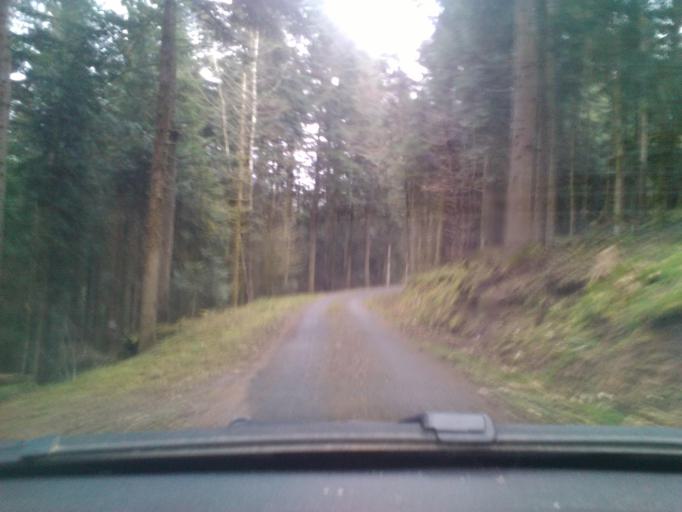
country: FR
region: Lorraine
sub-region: Departement des Vosges
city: Moyenmoutier
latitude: 48.3921
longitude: 6.8915
